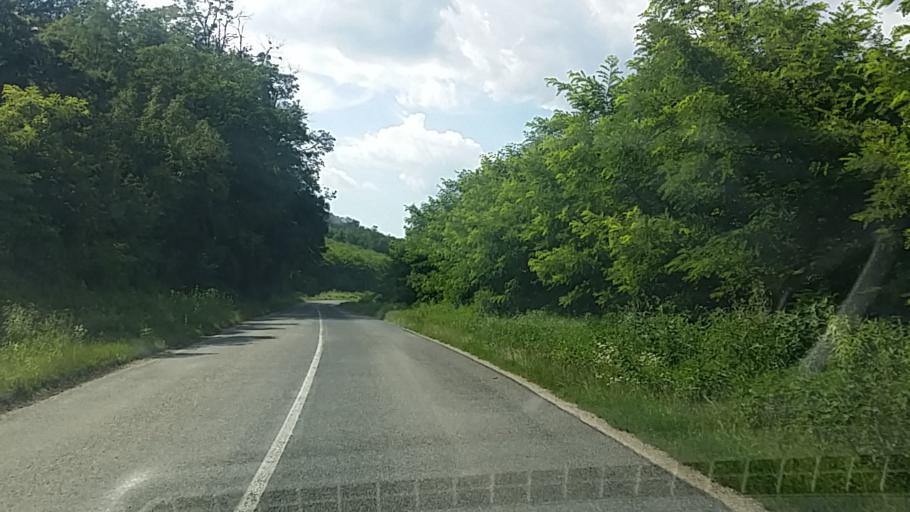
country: HU
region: Zala
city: Becsehely
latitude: 46.4645
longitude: 16.8050
